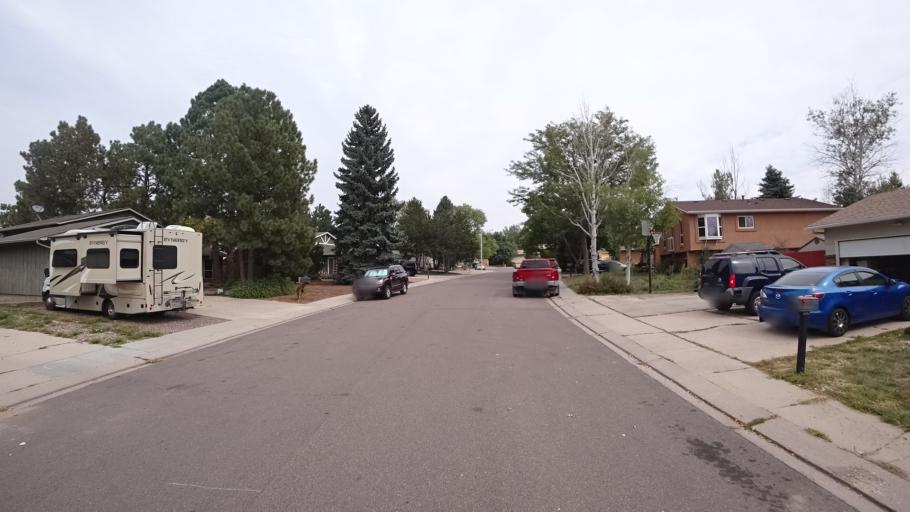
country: US
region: Colorado
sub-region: El Paso County
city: Cimarron Hills
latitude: 38.9003
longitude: -104.7348
